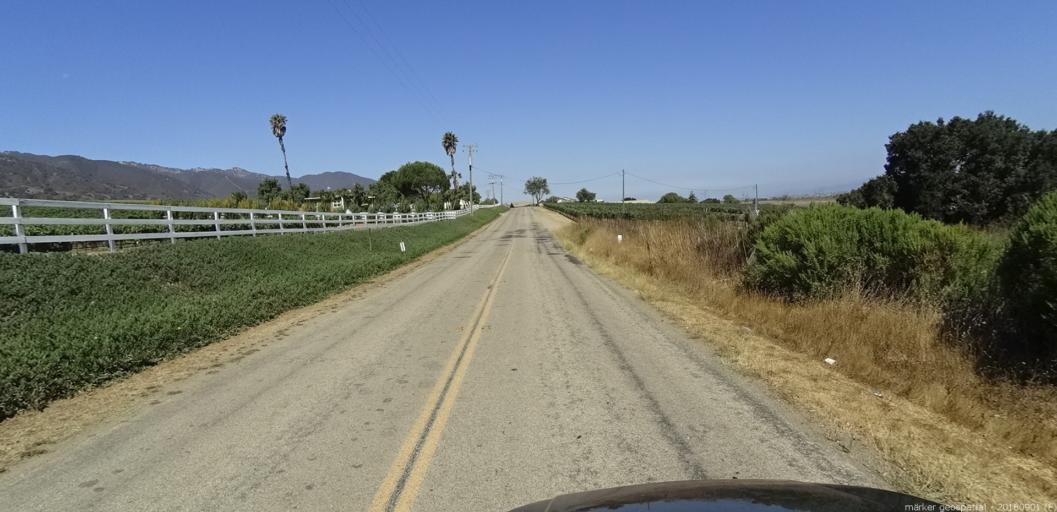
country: US
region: California
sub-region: Monterey County
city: Gonzales
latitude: 36.5020
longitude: -121.5049
